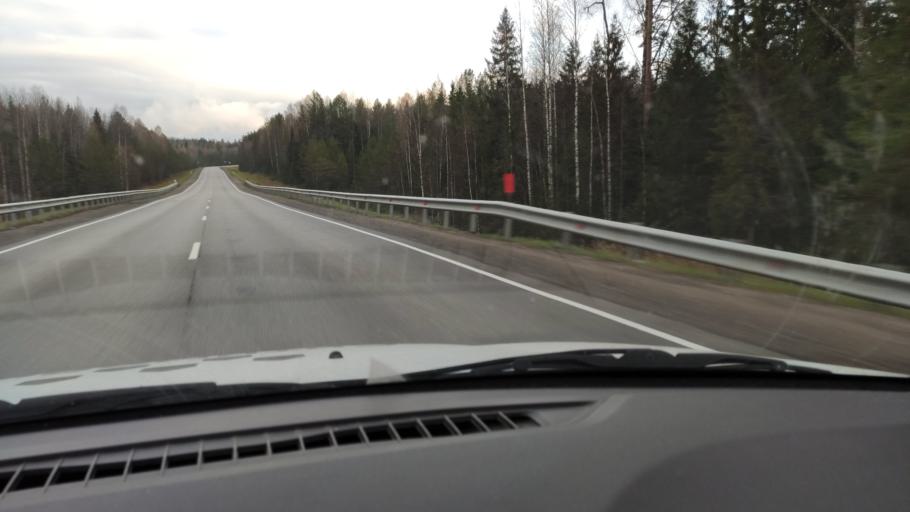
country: RU
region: Kirov
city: Chernaya Kholunitsa
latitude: 58.8234
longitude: 51.7972
